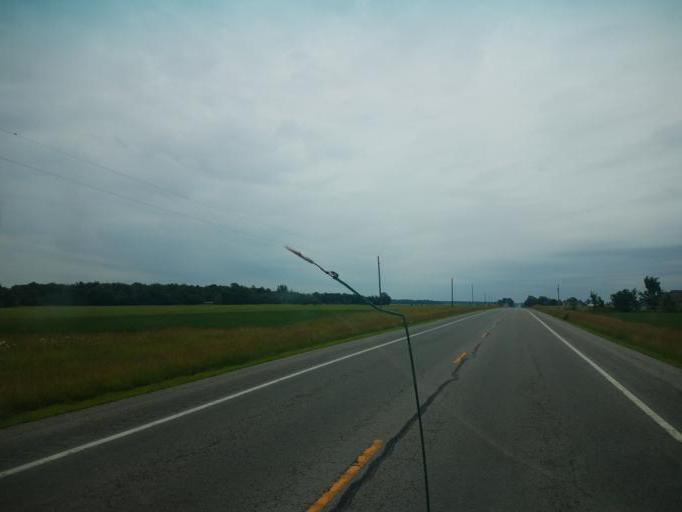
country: US
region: Ohio
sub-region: Hardin County
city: Kenton
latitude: 40.6880
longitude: -83.6891
